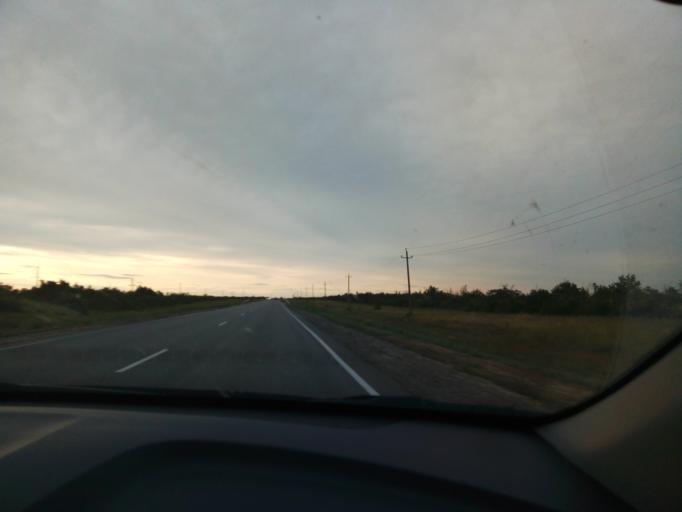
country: RU
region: Volgograd
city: Primorsk
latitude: 49.2931
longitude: 44.8637
